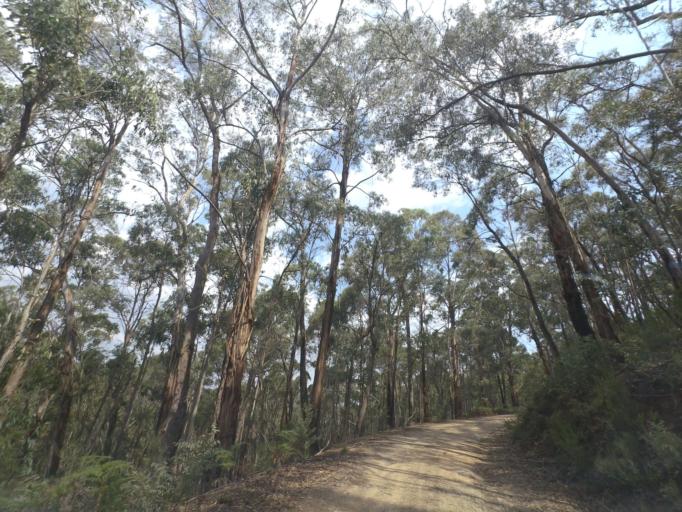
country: AU
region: Victoria
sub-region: Moorabool
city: Bacchus Marsh
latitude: -37.4685
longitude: 144.3945
